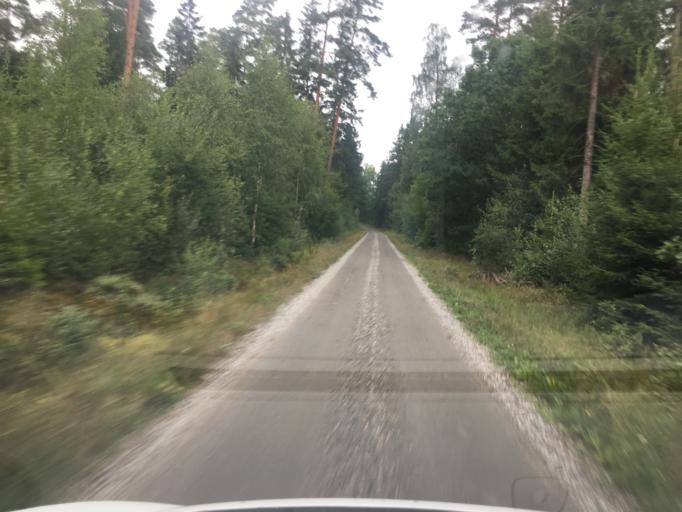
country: SE
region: Kronoberg
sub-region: Ljungby Kommun
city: Lagan
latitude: 56.9596
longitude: 14.0435
